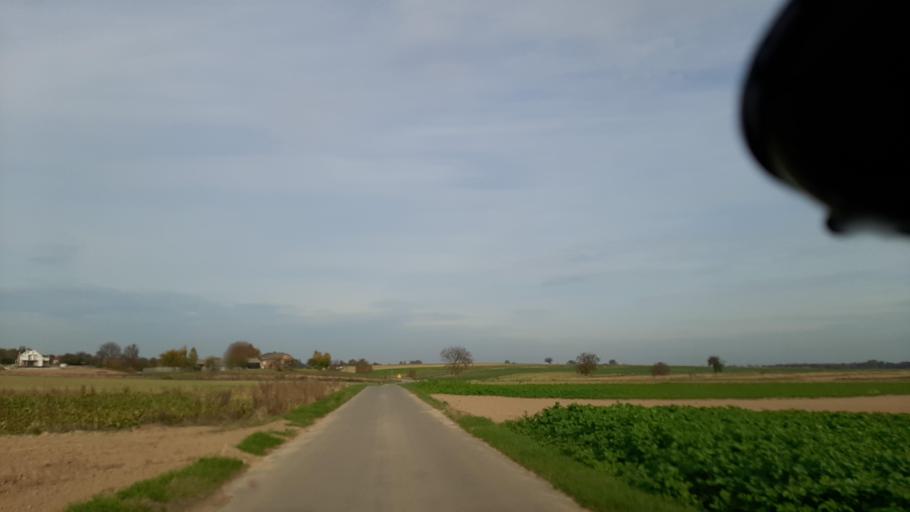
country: PL
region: Lublin Voivodeship
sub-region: Powiat lubelski
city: Jastkow
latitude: 51.3290
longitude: 22.4087
